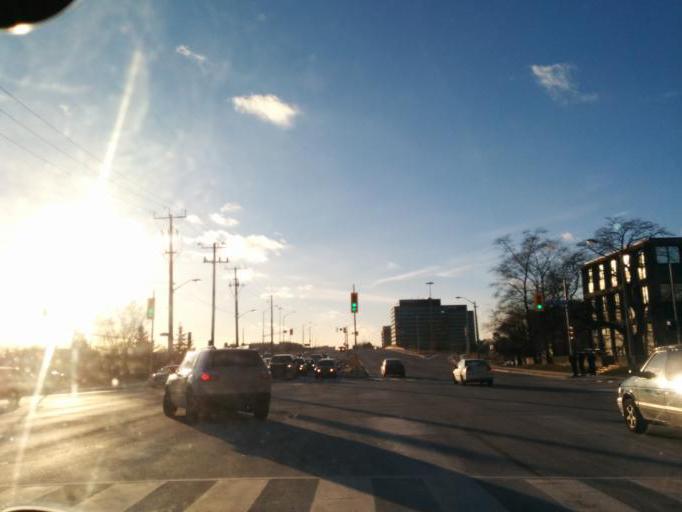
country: CA
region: Ontario
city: Etobicoke
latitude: 43.6464
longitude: -79.5596
